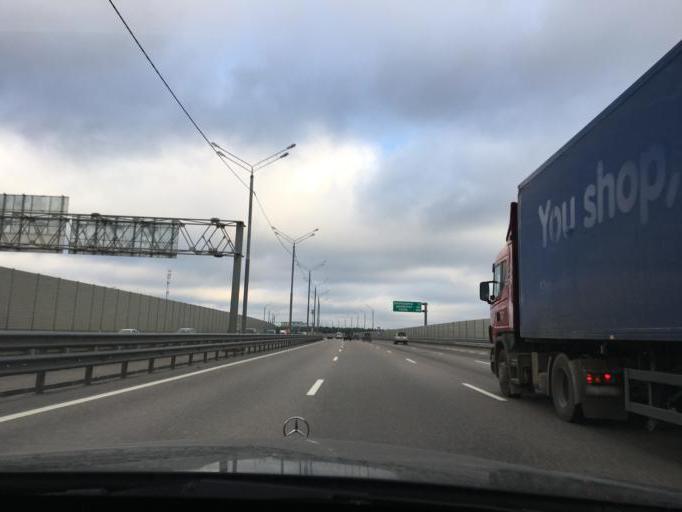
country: RU
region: Moskovskaya
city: Rozhdestveno
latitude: 55.8128
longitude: 37.0270
